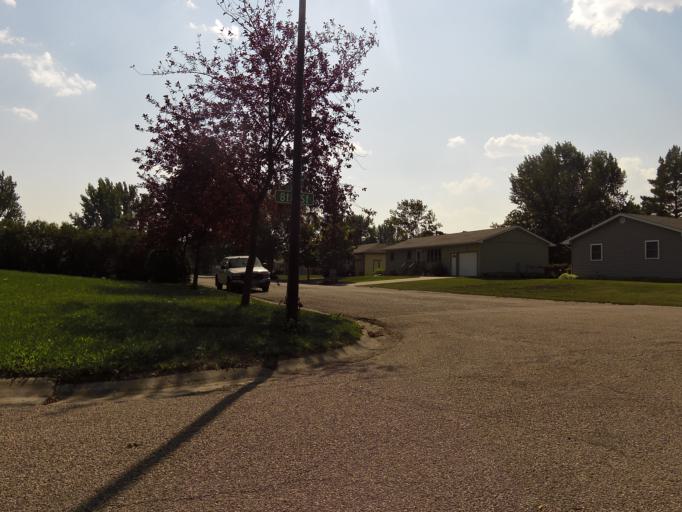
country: US
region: North Dakota
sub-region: Walsh County
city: Grafton
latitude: 48.4164
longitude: -97.3981
